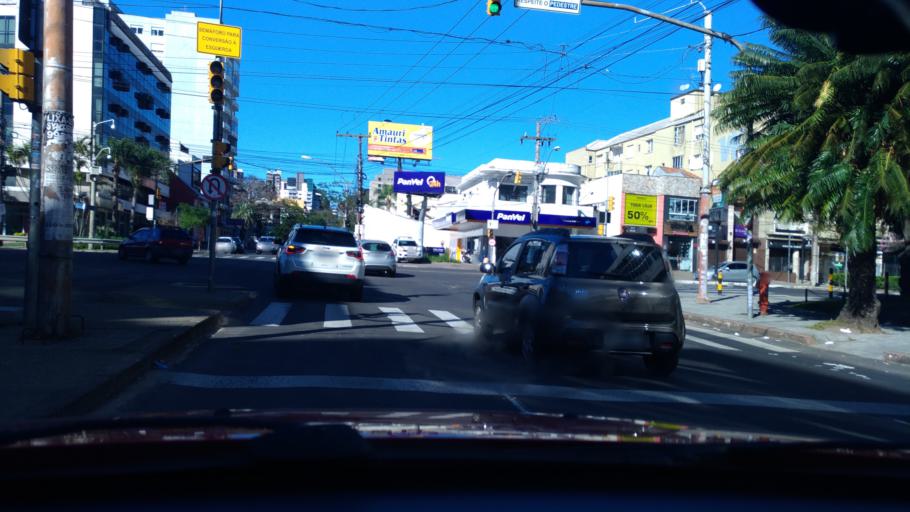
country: BR
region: Rio Grande do Sul
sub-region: Porto Alegre
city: Porto Alegre
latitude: -30.0180
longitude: -51.1981
